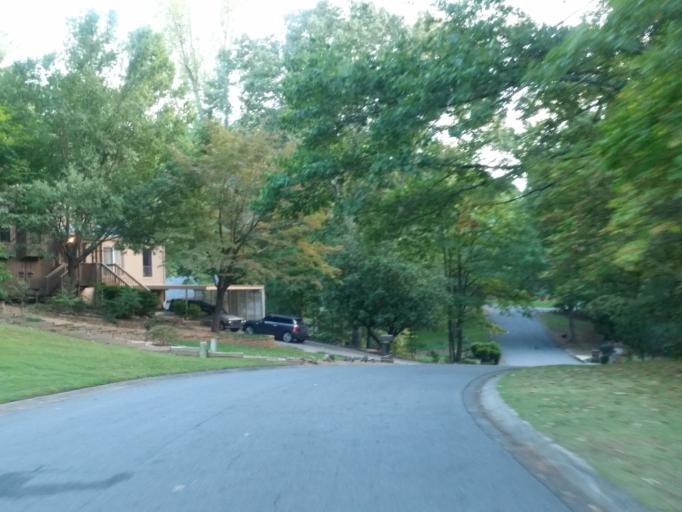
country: US
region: Georgia
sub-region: Cherokee County
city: Woodstock
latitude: 34.0161
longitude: -84.4734
